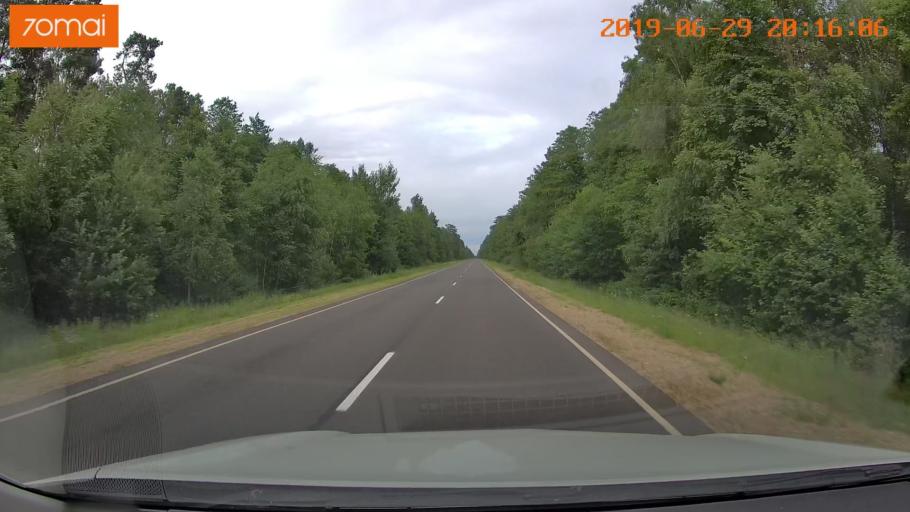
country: BY
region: Brest
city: Asnyezhytsy
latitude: 52.3789
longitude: 26.1894
